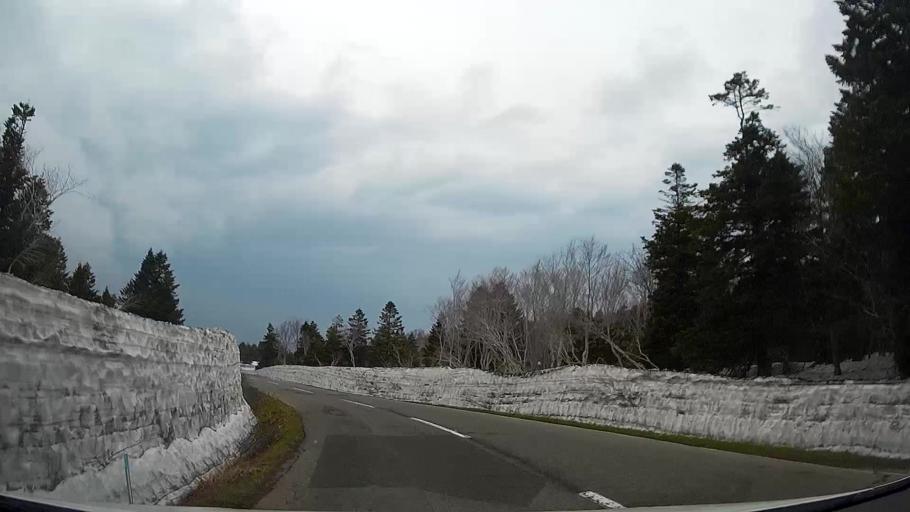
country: JP
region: Aomori
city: Aomori Shi
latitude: 40.6382
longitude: 140.8654
